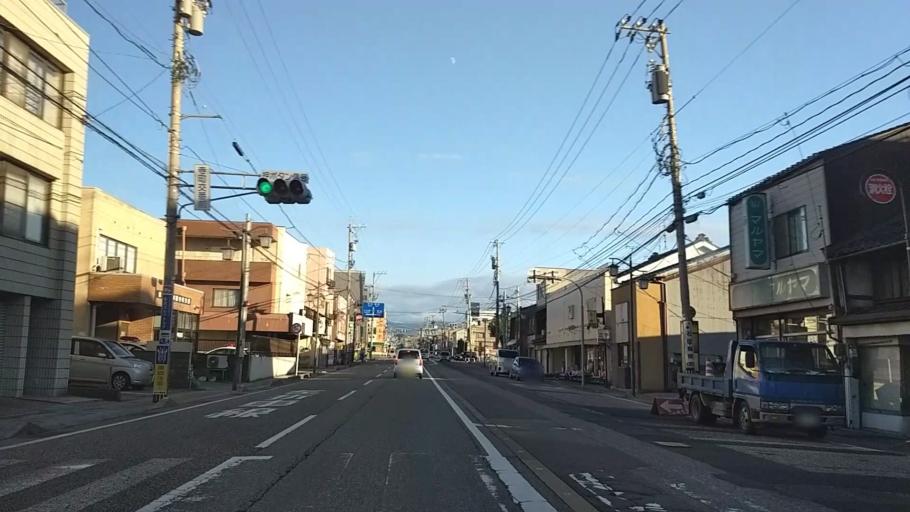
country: JP
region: Ishikawa
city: Nonoichi
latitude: 36.5473
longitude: 136.6584
